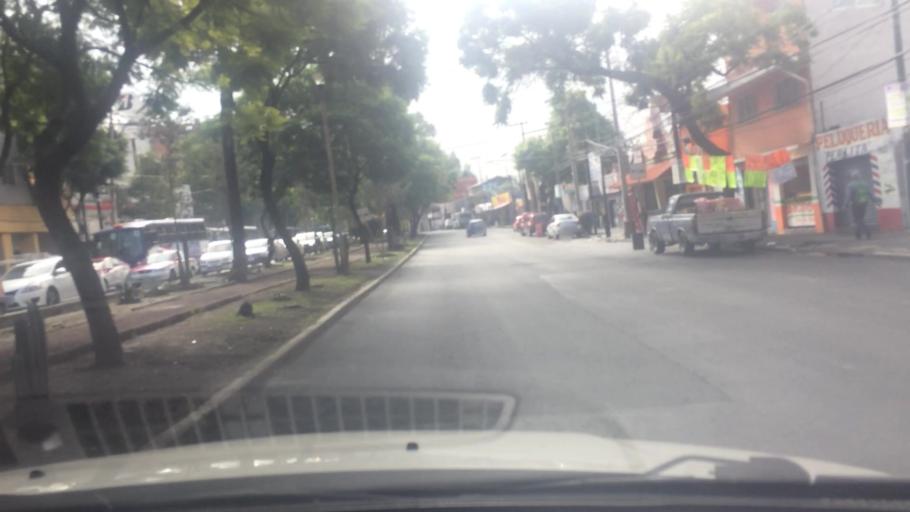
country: MX
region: Mexico City
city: Coyoacan
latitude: 19.3374
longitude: -99.1224
